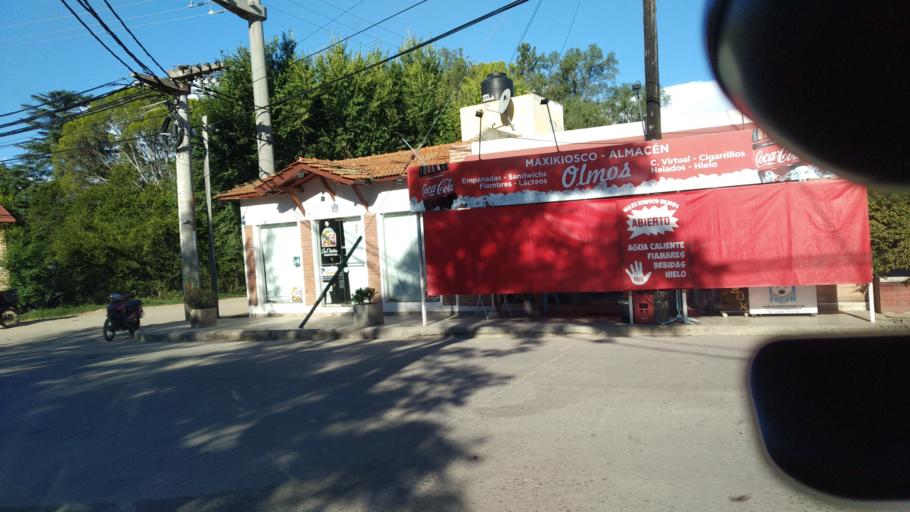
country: AR
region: Cordoba
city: Mina Clavero
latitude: -31.7281
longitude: -65.0000
